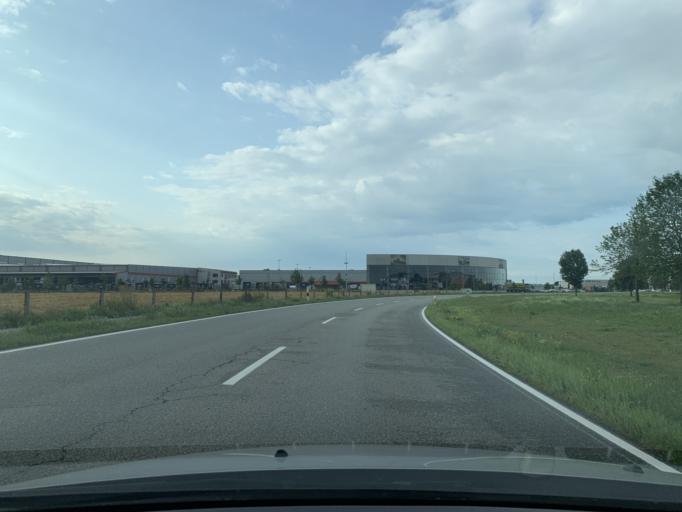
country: DE
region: Bavaria
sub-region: Upper Bavaria
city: Muehldorf
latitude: 48.2574
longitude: 12.5468
